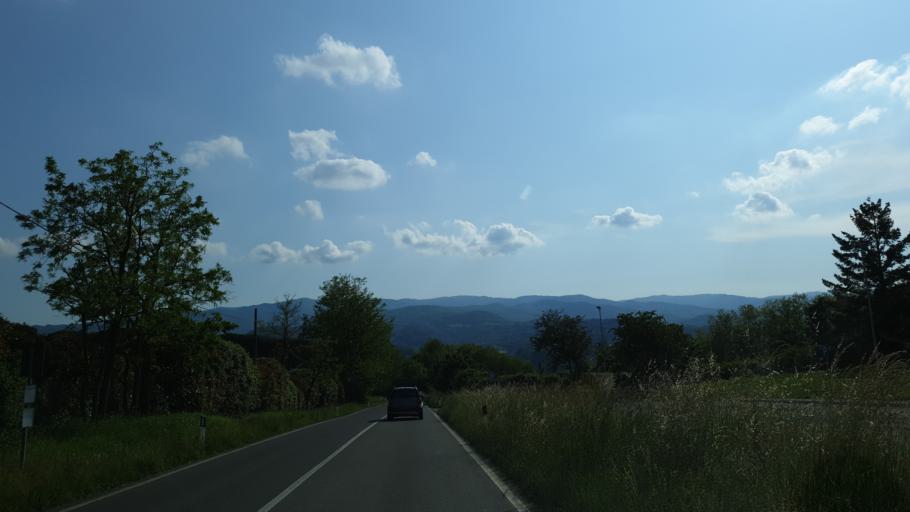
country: IT
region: Tuscany
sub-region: Province of Arezzo
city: Soci
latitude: 43.7307
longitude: 11.7892
